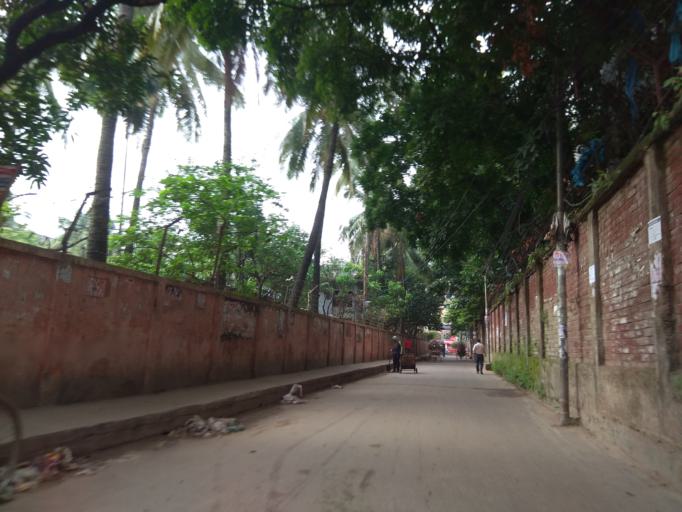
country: BD
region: Dhaka
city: Azimpur
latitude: 23.8076
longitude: 90.3662
